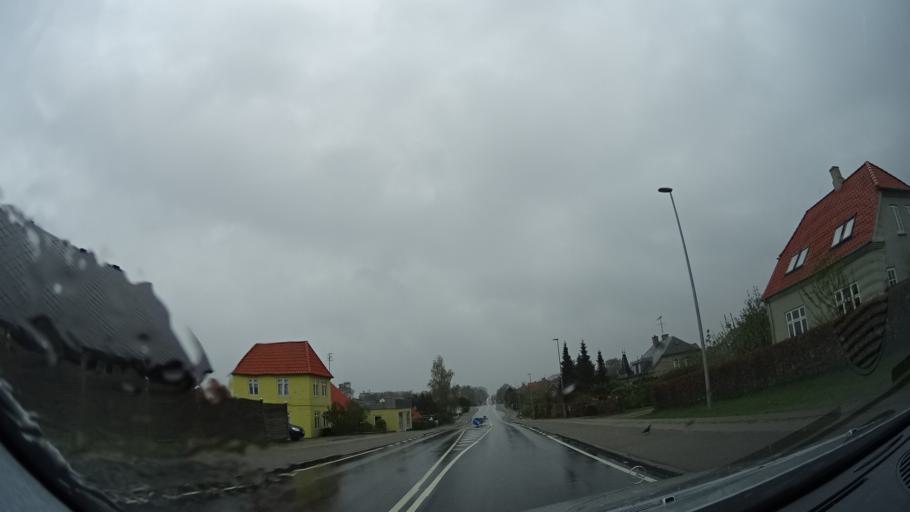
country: DK
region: Zealand
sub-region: Holbaek Kommune
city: Holbaek
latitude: 55.7152
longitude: 11.6818
